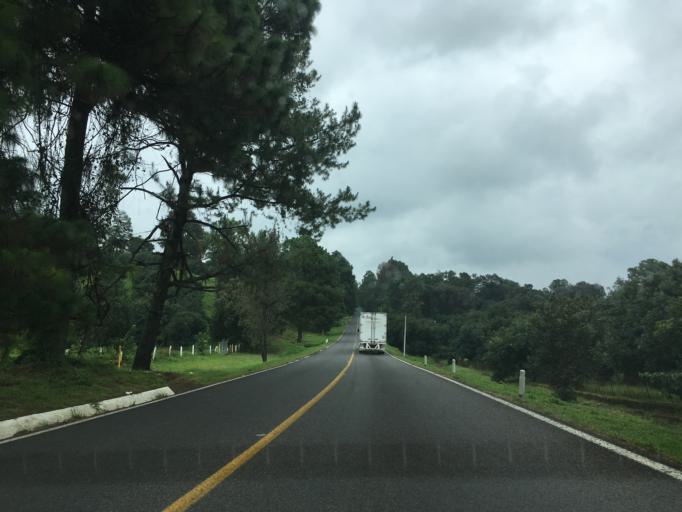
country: MX
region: Michoacan
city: Tingambato
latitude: 19.4754
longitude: -101.9042
